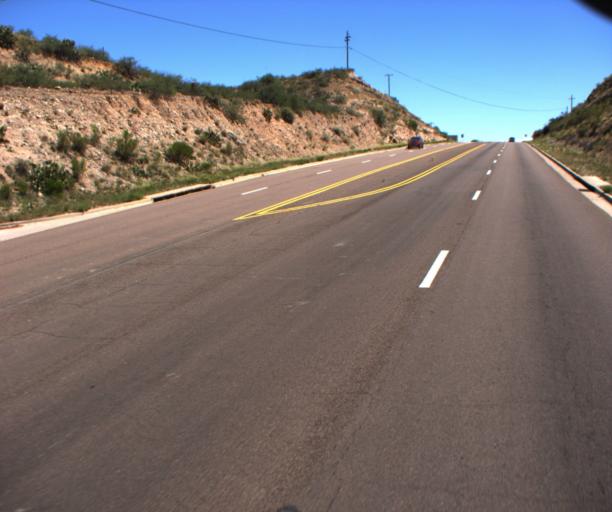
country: US
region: Arizona
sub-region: Gila County
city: Globe
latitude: 33.3936
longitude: -110.7613
